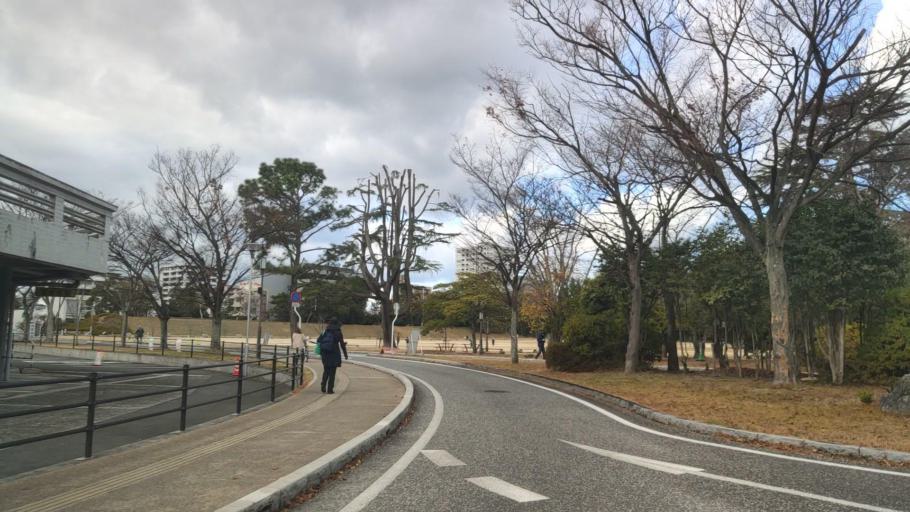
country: JP
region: Ehime
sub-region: Shikoku-chuo Shi
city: Matsuyama
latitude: 33.8413
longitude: 132.7614
